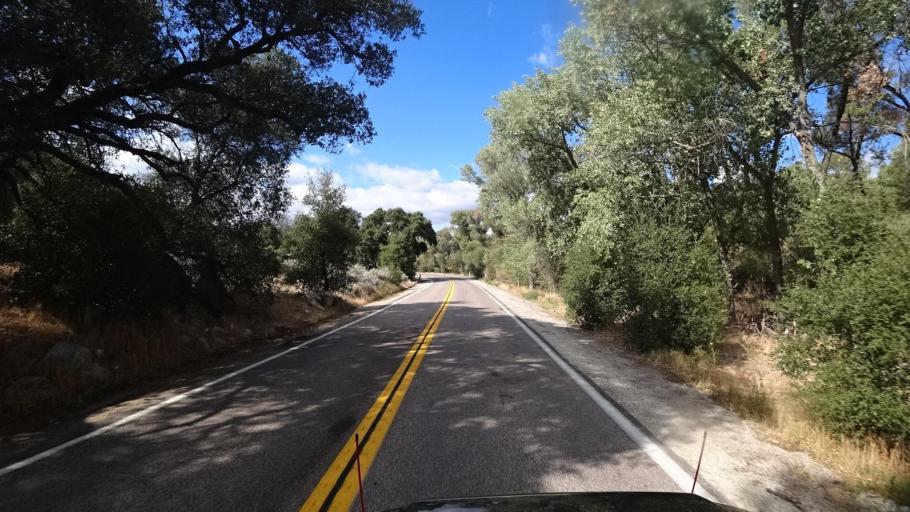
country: US
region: California
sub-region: San Diego County
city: Campo
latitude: 32.7075
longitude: -116.4909
